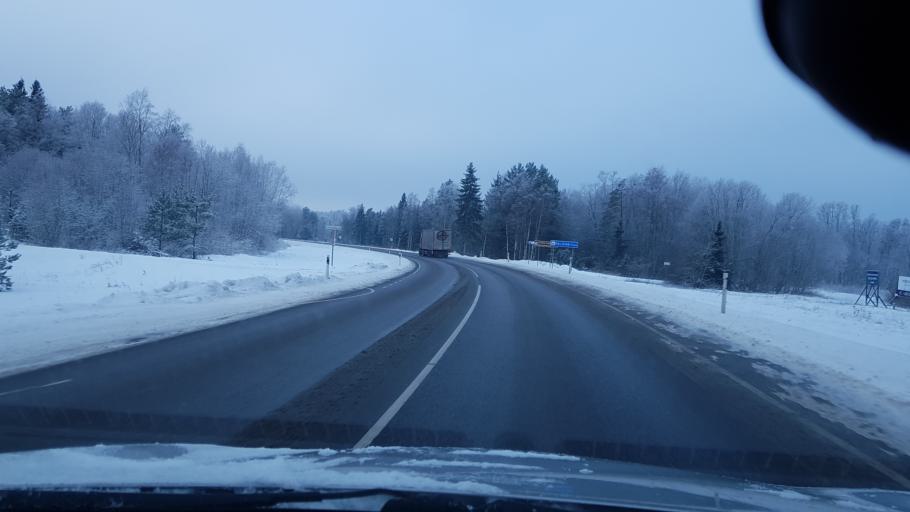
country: EE
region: Harju
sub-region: Paldiski linn
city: Paldiski
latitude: 59.3450
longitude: 24.1852
